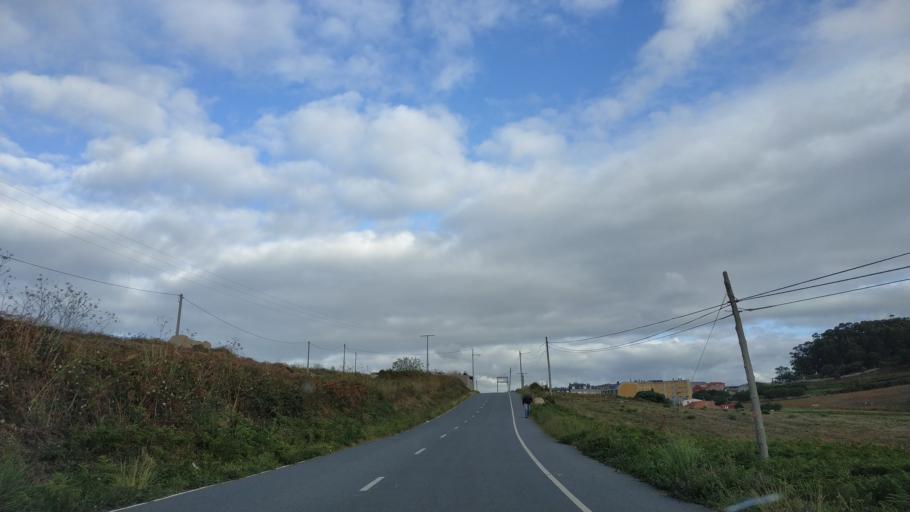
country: ES
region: Galicia
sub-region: Provincia da Coruna
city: A Coruna
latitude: 43.3707
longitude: -8.4383
